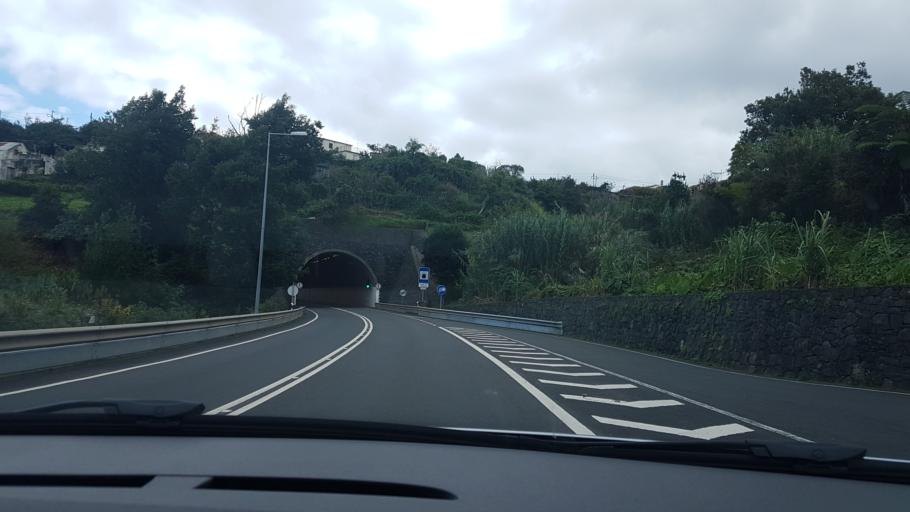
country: PT
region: Madeira
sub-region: Santana
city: Santana
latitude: 32.8099
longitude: -16.8815
